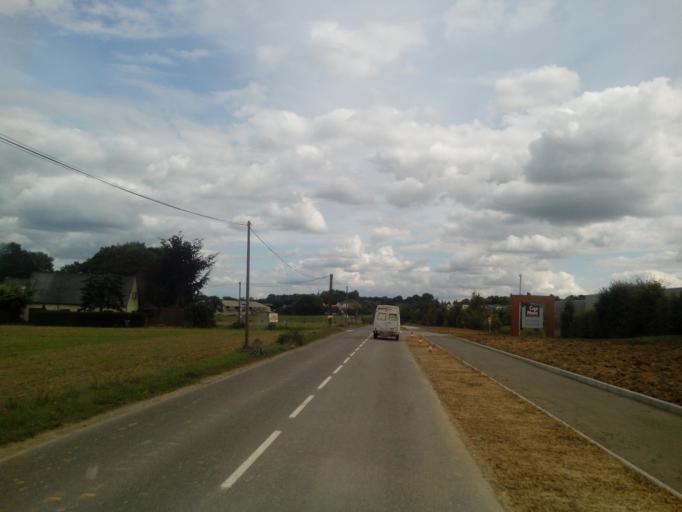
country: FR
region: Brittany
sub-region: Departement d'Ille-et-Vilaine
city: La Chapelle-des-Fougeretz
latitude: 48.2013
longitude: -1.7238
